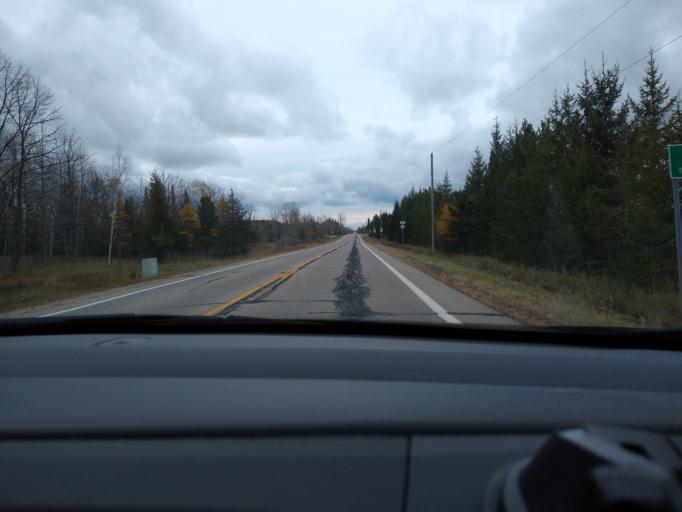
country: US
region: Michigan
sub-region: Delta County
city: Escanaba
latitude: 45.7795
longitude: -87.3251
